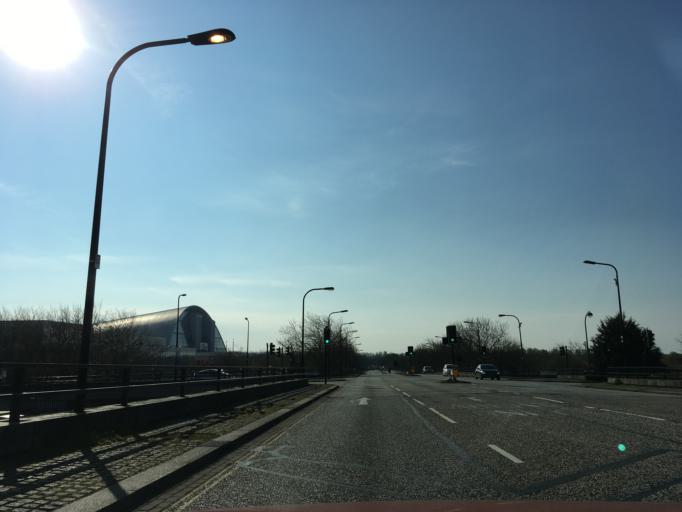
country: GB
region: England
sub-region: Milton Keynes
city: Milton Keynes
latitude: 52.0434
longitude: -0.7544
